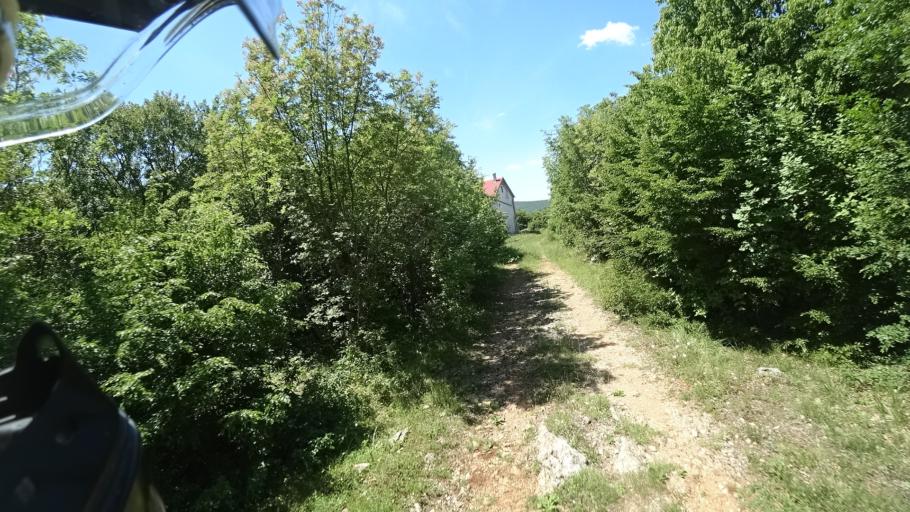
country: HR
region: Sibensko-Kniniska
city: Knin
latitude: 44.0046
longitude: 16.3082
